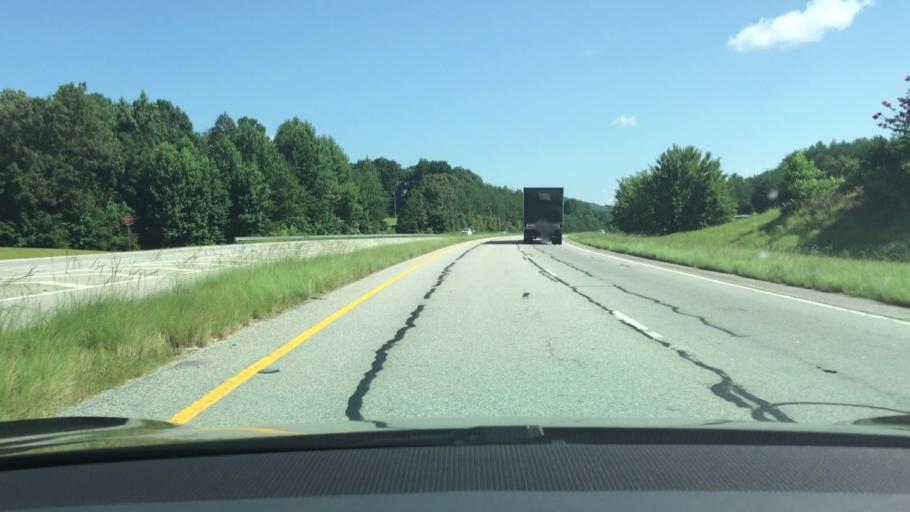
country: US
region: Georgia
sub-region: Habersham County
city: Clarkesville
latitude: 34.6889
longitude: -83.4242
